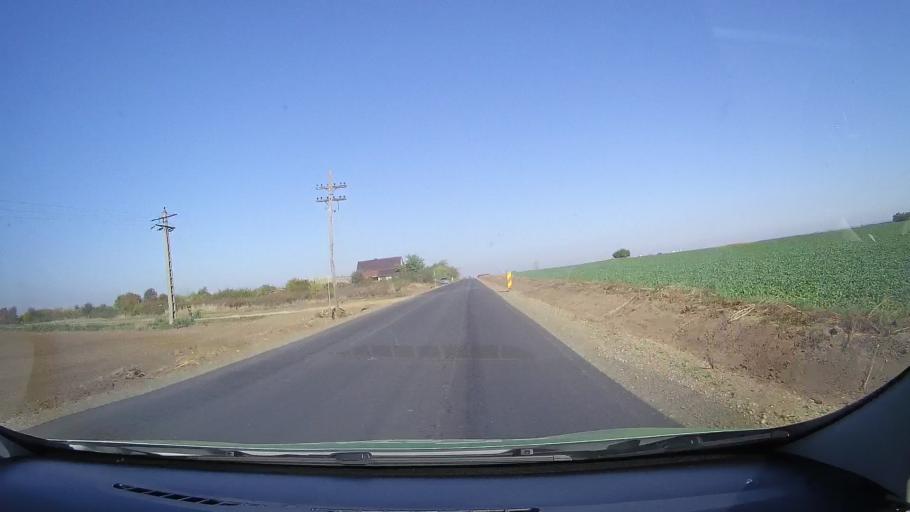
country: RO
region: Satu Mare
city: Carei
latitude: 47.6568
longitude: 22.4605
